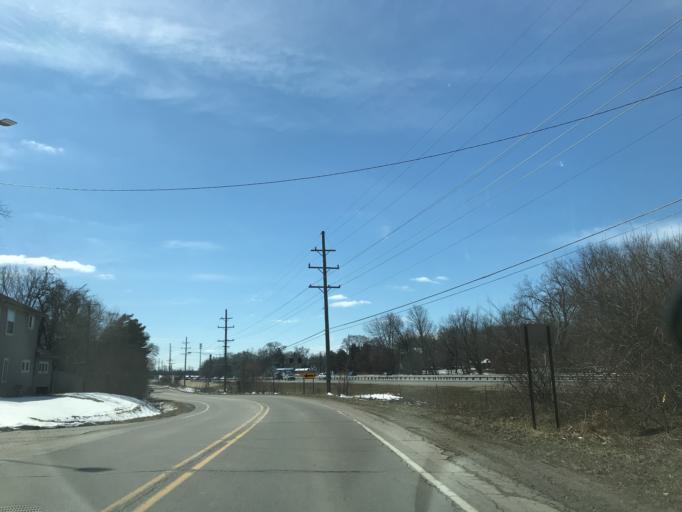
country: US
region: Michigan
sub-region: Livingston County
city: Whitmore Lake
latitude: 42.4036
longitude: -83.7620
